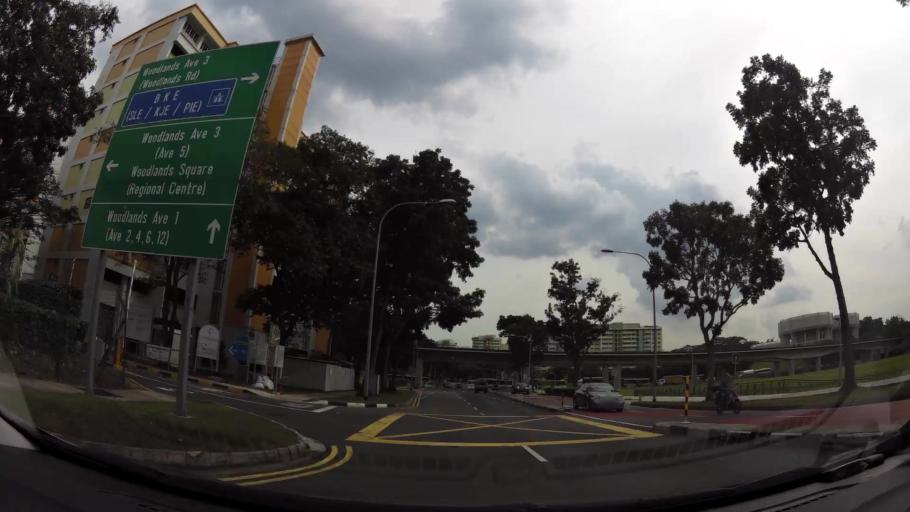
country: MY
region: Johor
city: Johor Bahru
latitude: 1.4336
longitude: 103.7727
